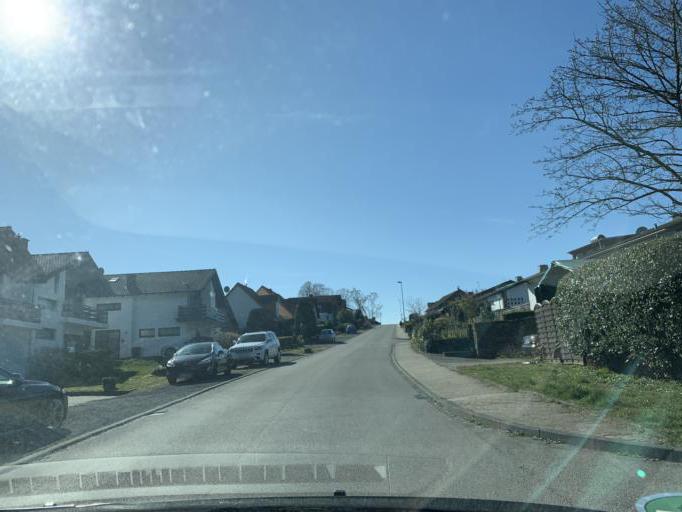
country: DE
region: North Rhine-Westphalia
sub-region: Regierungsbezirk Koln
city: Nideggen
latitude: 50.6939
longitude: 6.4880
